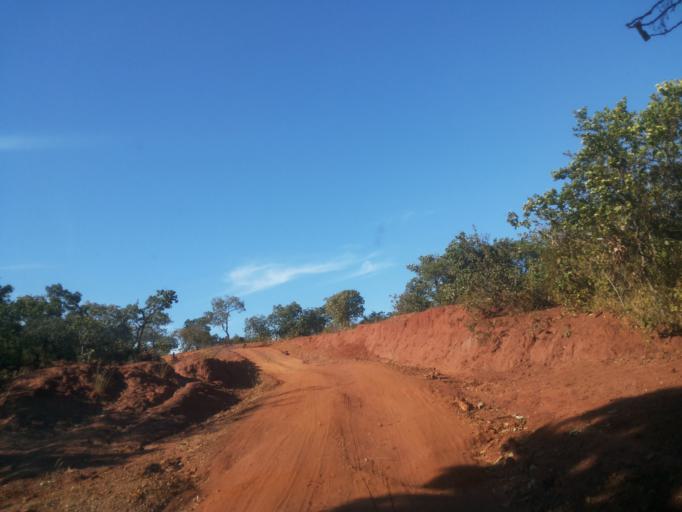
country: BR
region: Minas Gerais
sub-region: Ituiutaba
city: Ituiutaba
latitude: -19.1124
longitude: -49.4126
